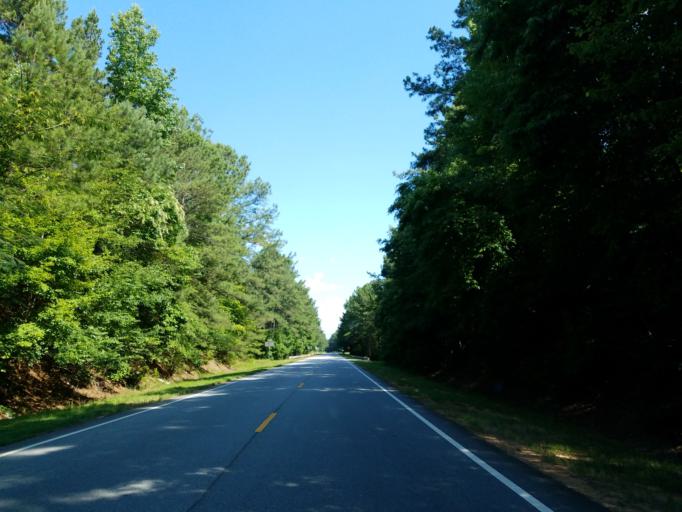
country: US
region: Georgia
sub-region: Crawford County
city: Roberta
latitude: 32.8520
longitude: -84.0761
